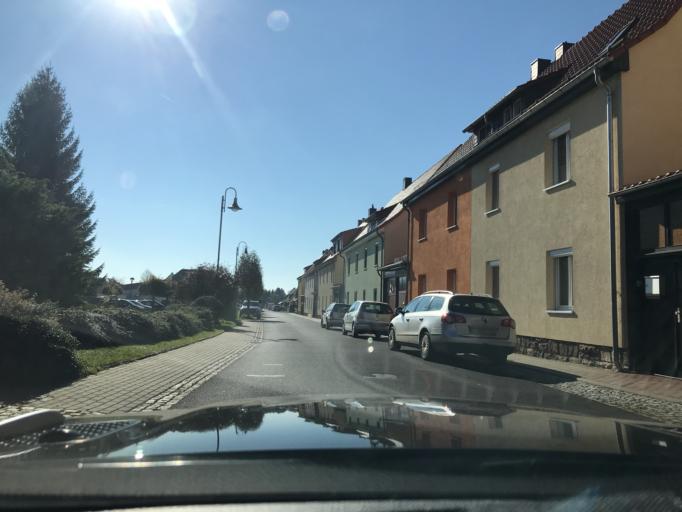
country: DE
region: Thuringia
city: Muehlhausen
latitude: 51.2341
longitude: 10.4535
